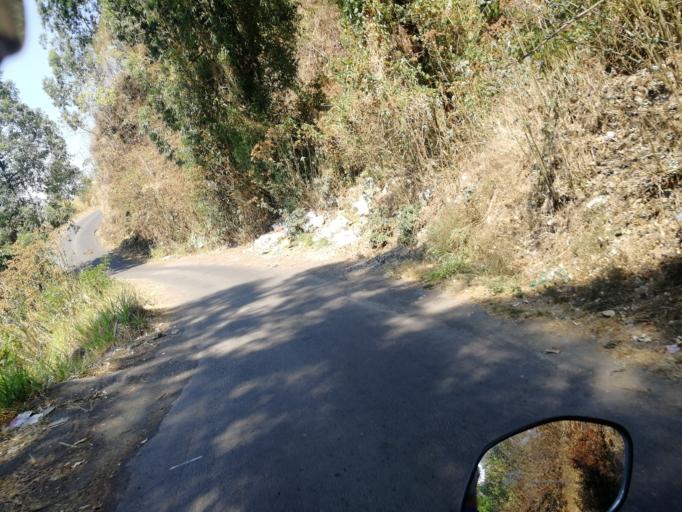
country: ID
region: Bali
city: Banjar Buahan
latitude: -8.2860
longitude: 115.4003
